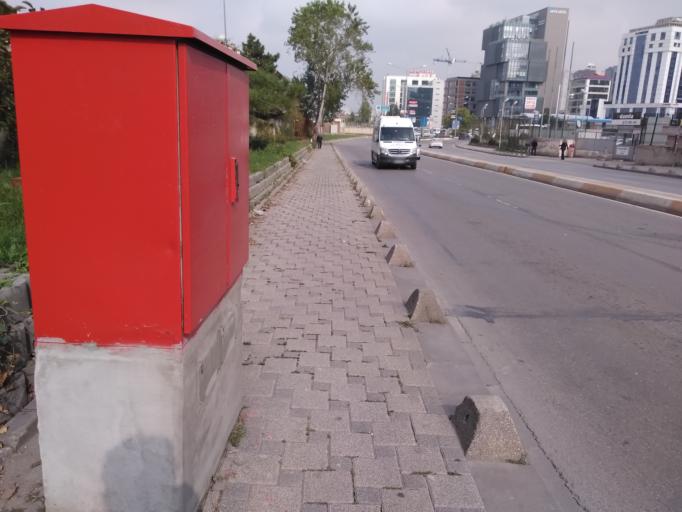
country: TR
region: Istanbul
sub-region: Atasehir
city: Atasehir
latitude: 40.9812
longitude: 29.1043
